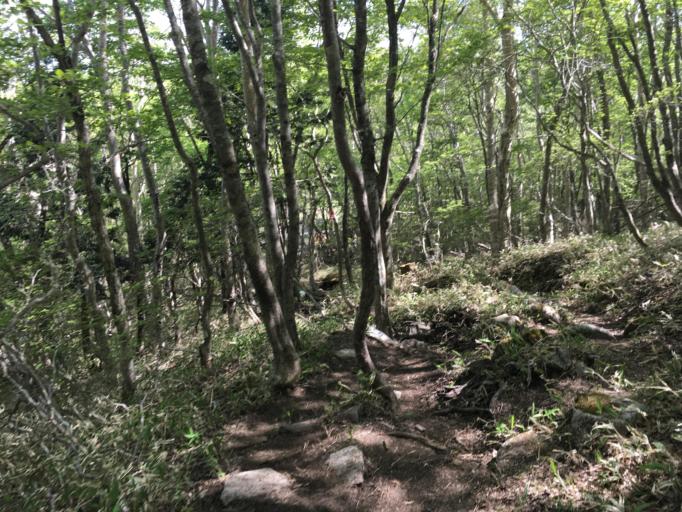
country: JP
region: Iwate
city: Ofunato
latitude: 39.1887
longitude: 141.7312
